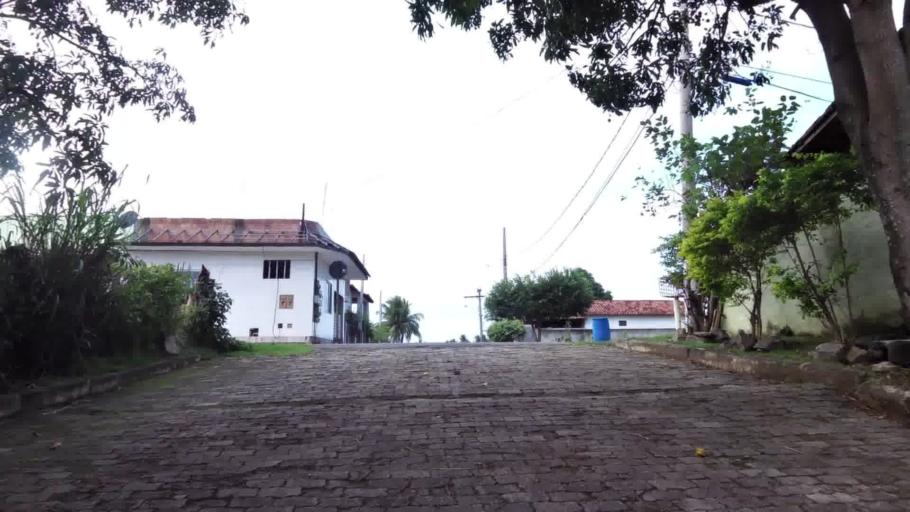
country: BR
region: Espirito Santo
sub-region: Piuma
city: Piuma
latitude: -20.8271
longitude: -40.6978
